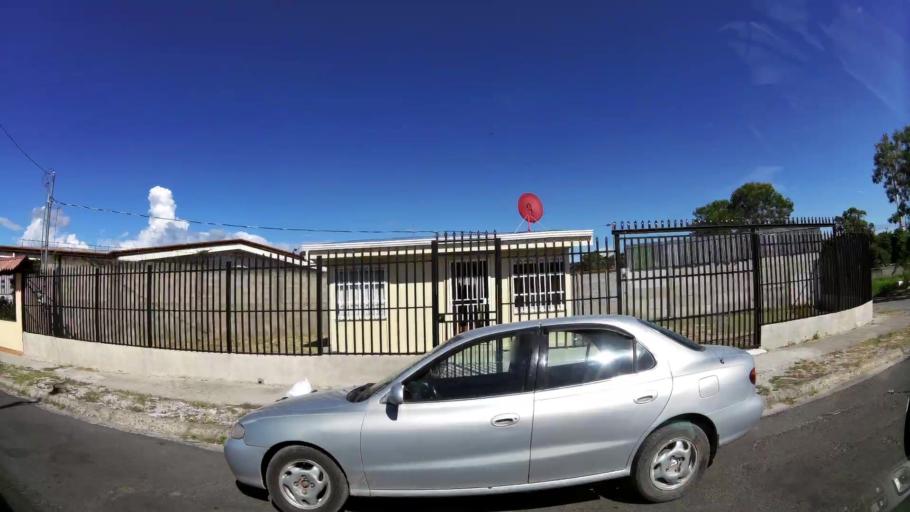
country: CR
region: Guanacaste
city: Liberia
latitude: 10.6385
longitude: -85.4368
